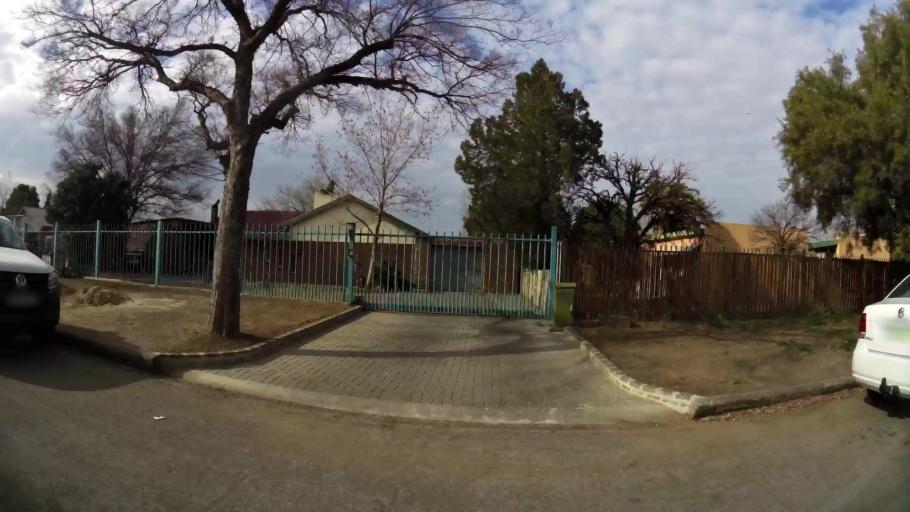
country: ZA
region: Orange Free State
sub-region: Mangaung Metropolitan Municipality
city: Bloemfontein
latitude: -29.0878
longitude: 26.2502
